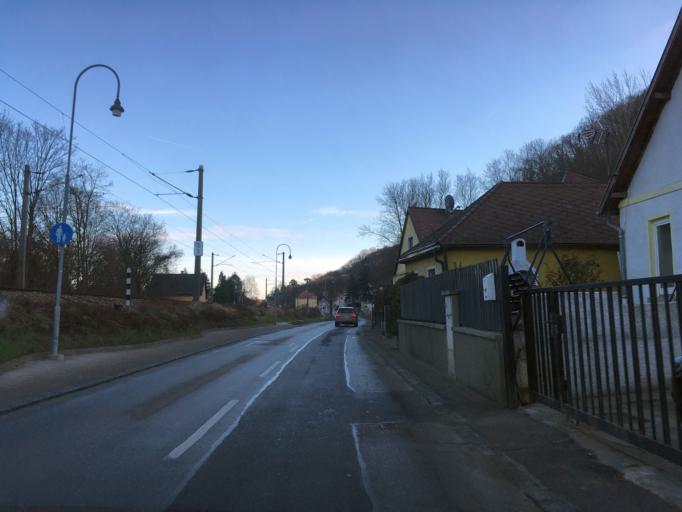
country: AT
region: Lower Austria
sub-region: Politischer Bezirk Korneuburg
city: Spillern
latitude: 48.3495
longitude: 16.2761
